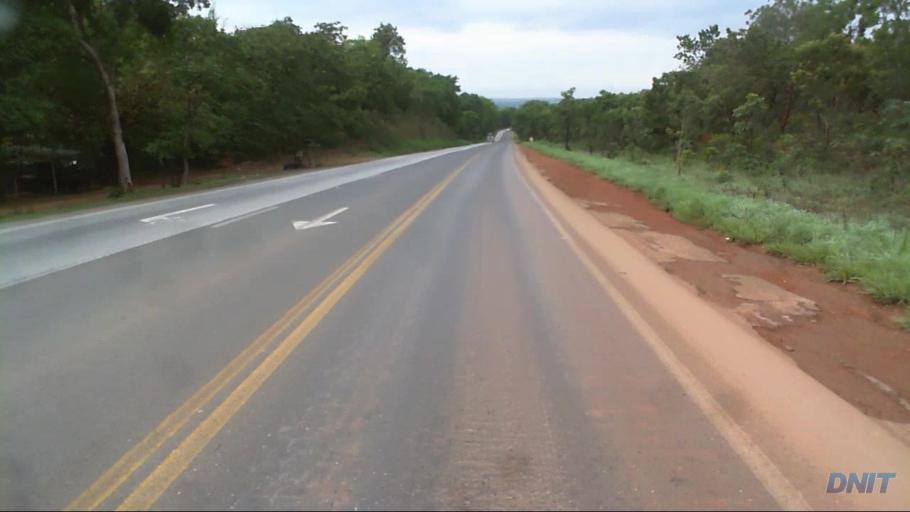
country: BR
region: Goias
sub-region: Uruacu
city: Uruacu
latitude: -14.5654
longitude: -49.1562
